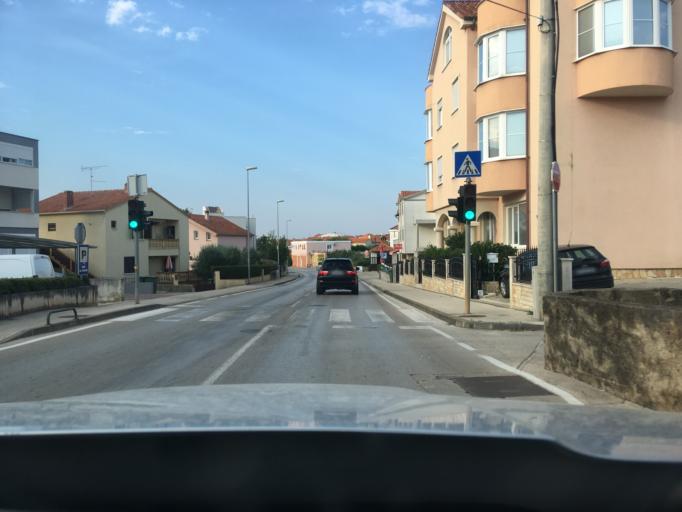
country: HR
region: Zadarska
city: Zadar
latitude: 44.1330
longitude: 15.2308
